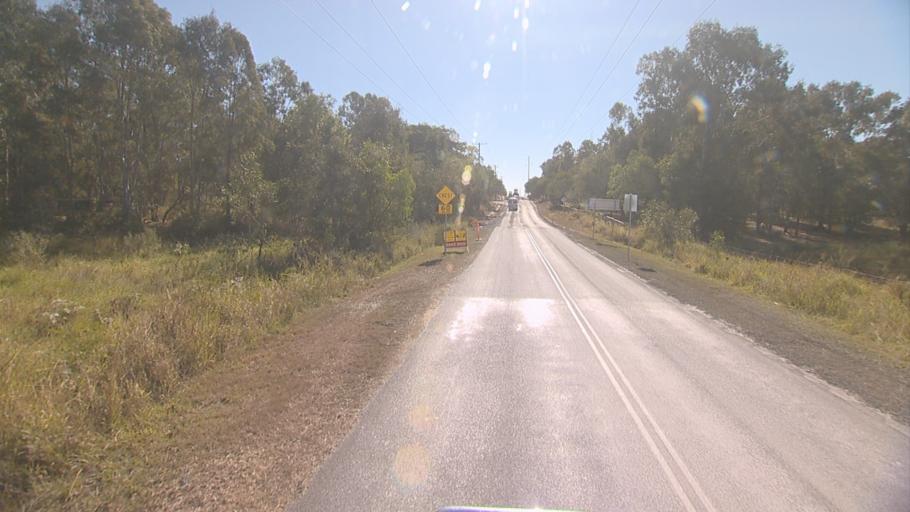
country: AU
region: Queensland
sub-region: Logan
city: Cedar Vale
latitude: -27.8590
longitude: 153.0194
